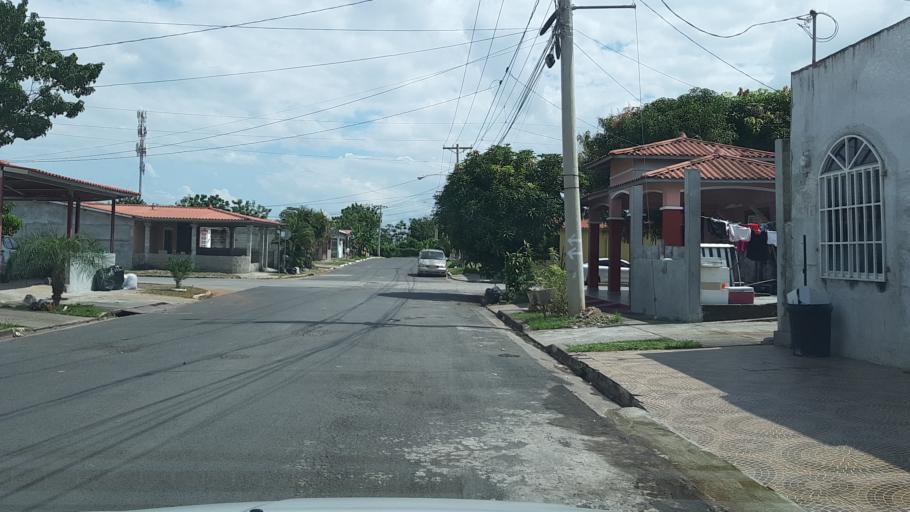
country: PA
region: Panama
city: Tocumen
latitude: 9.0718
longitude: -79.3620
